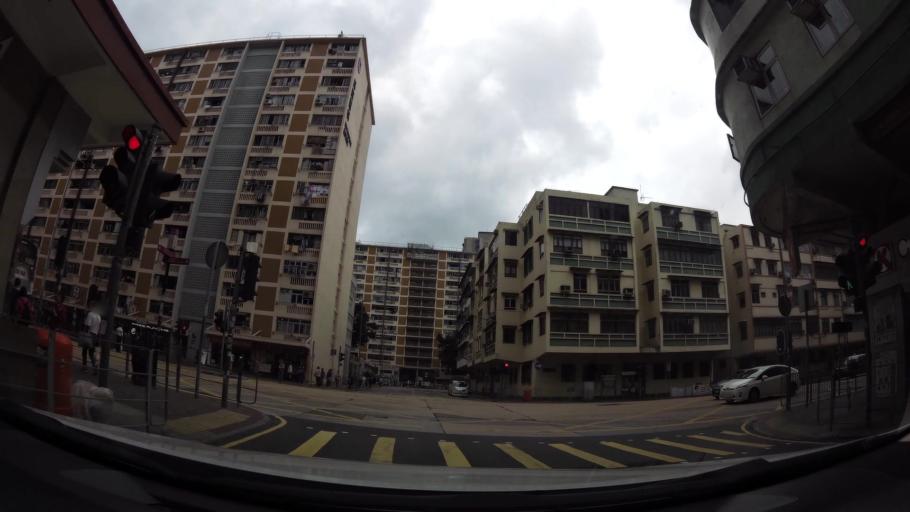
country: HK
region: Kowloon City
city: Kowloon
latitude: 22.3227
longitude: 114.1881
